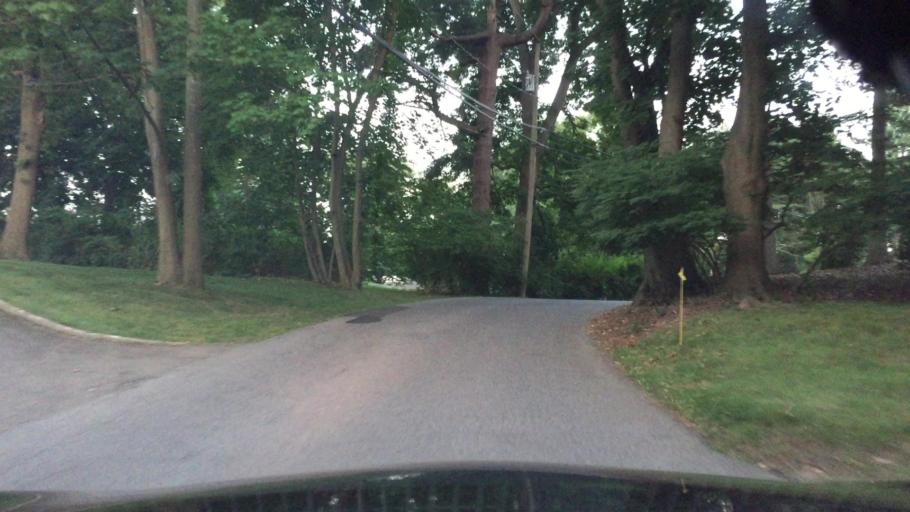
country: US
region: Connecticut
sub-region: Fairfield County
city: Darien
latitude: 41.0699
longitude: -73.4269
